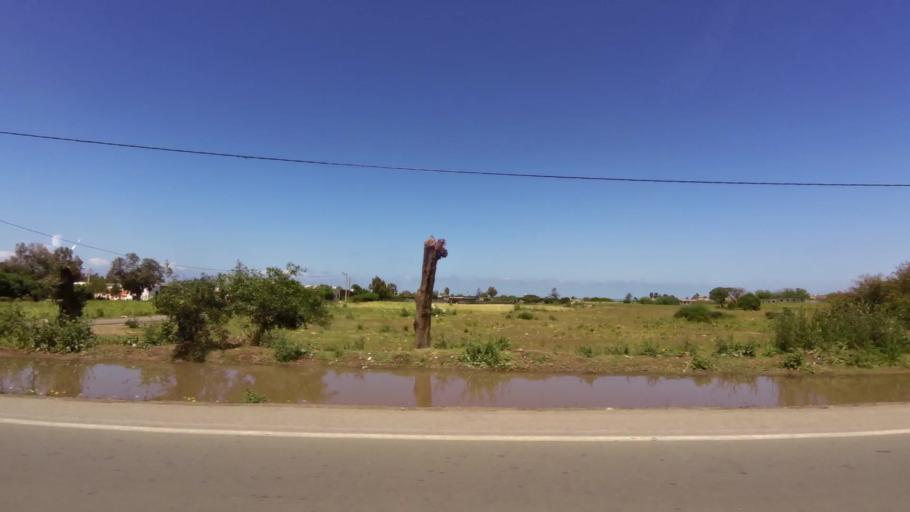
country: MA
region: Grand Casablanca
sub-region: Nouaceur
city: Dar Bouazza
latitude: 33.5169
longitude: -7.8044
